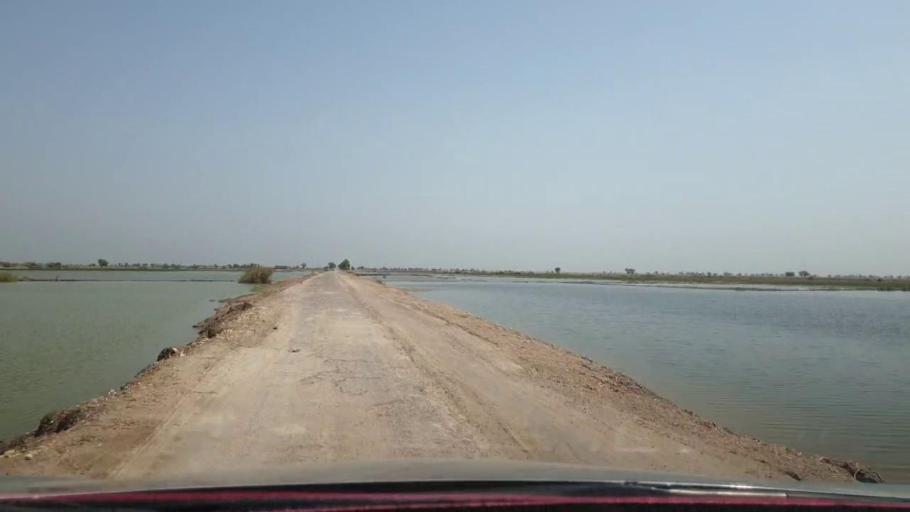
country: PK
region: Sindh
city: Warah
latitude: 27.3863
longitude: 67.7808
